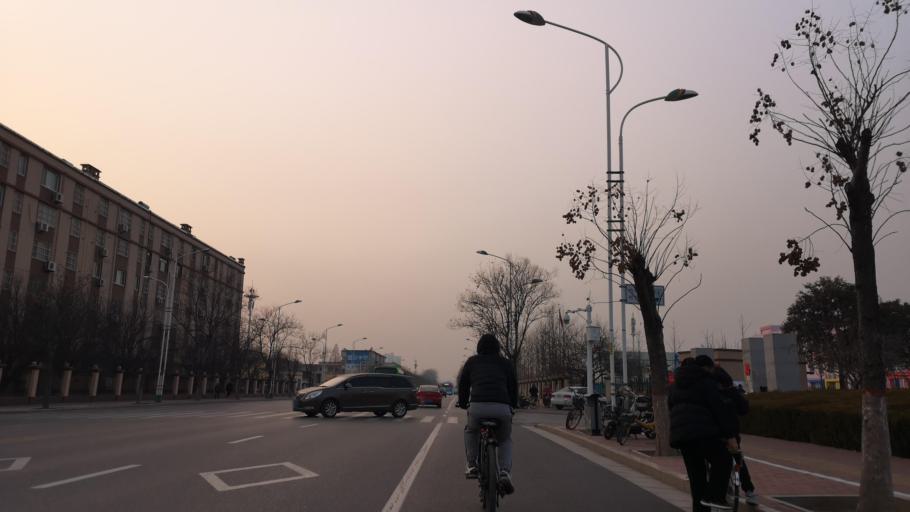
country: CN
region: Henan Sheng
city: Zhongyuanlu
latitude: 35.7840
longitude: 115.0790
